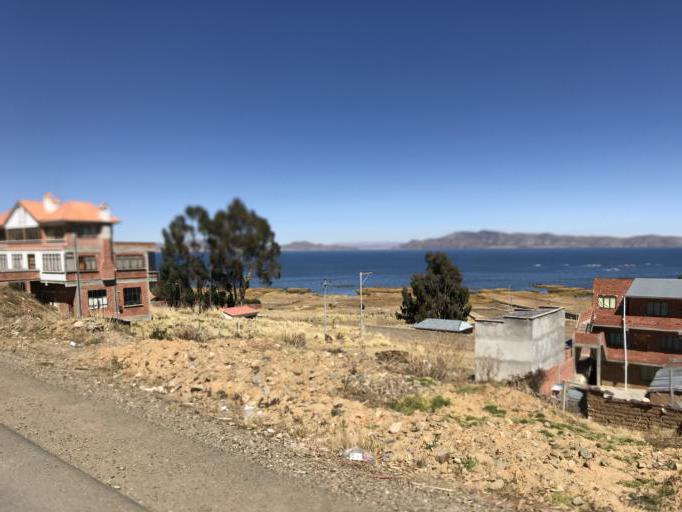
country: BO
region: La Paz
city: Huarina
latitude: -16.2148
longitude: -68.6498
